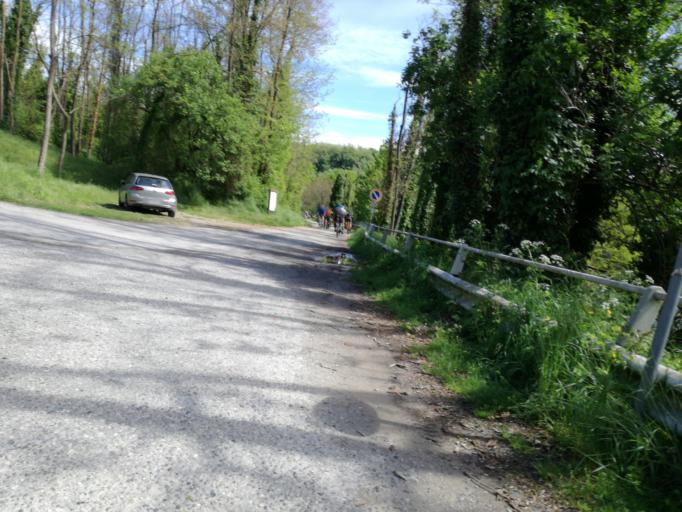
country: IT
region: Lombardy
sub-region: Provincia di Monza e Brianza
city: Porto d'Adda
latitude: 45.6539
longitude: 9.4847
